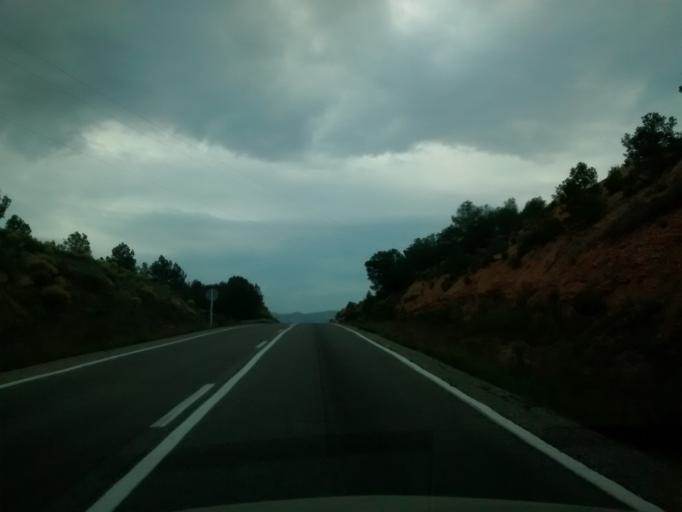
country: ES
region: Catalonia
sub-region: Provincia de Tarragona
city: Benifallet
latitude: 40.9981
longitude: 0.5153
